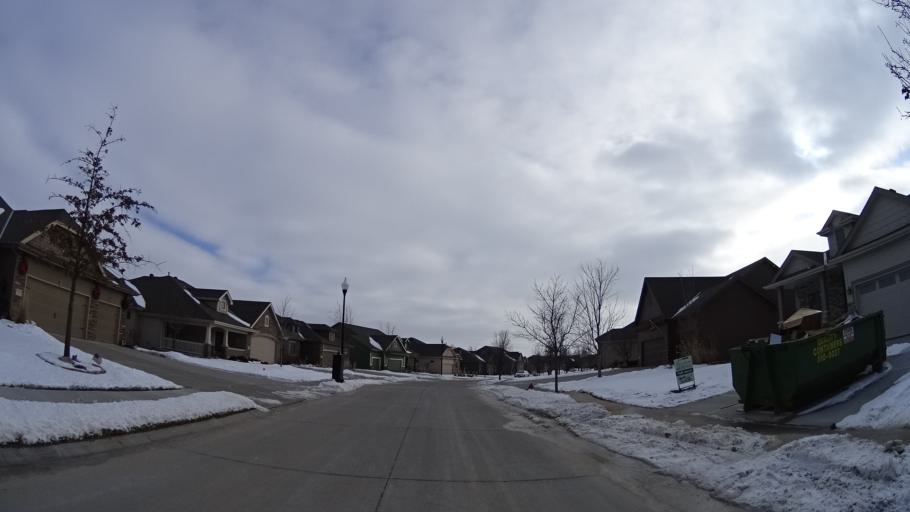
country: US
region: Nebraska
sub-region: Sarpy County
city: Papillion
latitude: 41.1254
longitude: -96.0254
